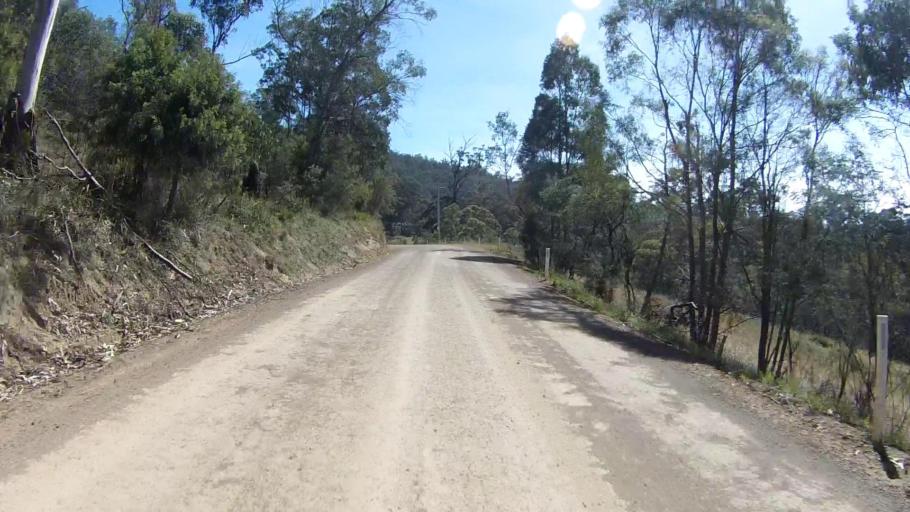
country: AU
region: Tasmania
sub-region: Sorell
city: Sorell
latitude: -42.7572
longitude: 147.6821
